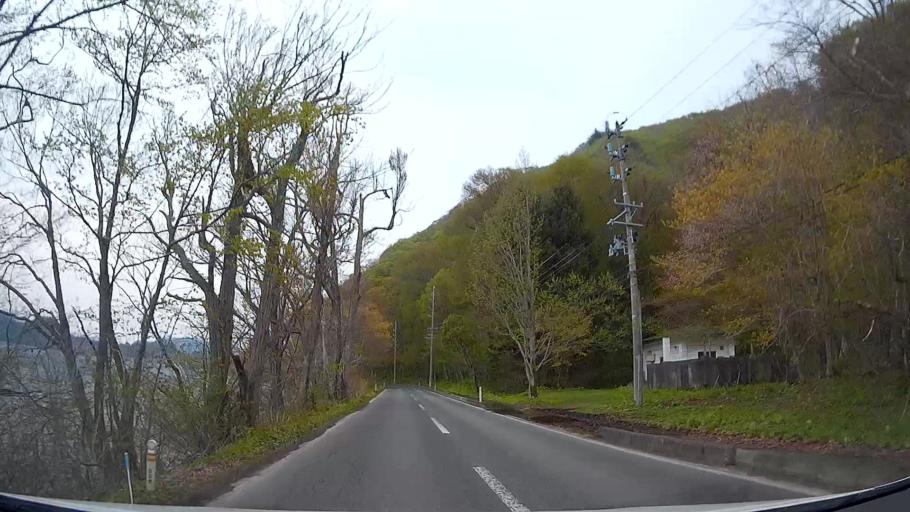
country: JP
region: Akita
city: Hanawa
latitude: 40.4163
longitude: 140.8871
